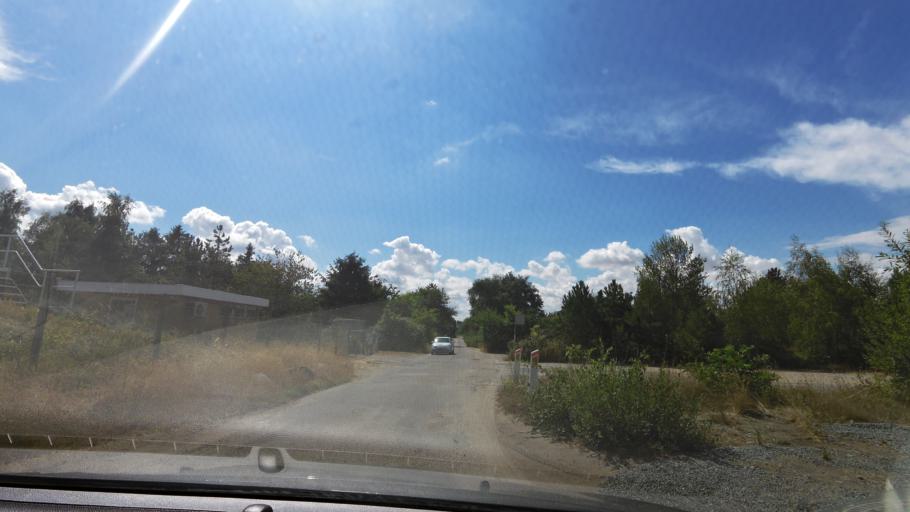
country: DK
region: South Denmark
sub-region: Nordfyns Kommune
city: Otterup
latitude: 55.5489
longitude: 10.4916
